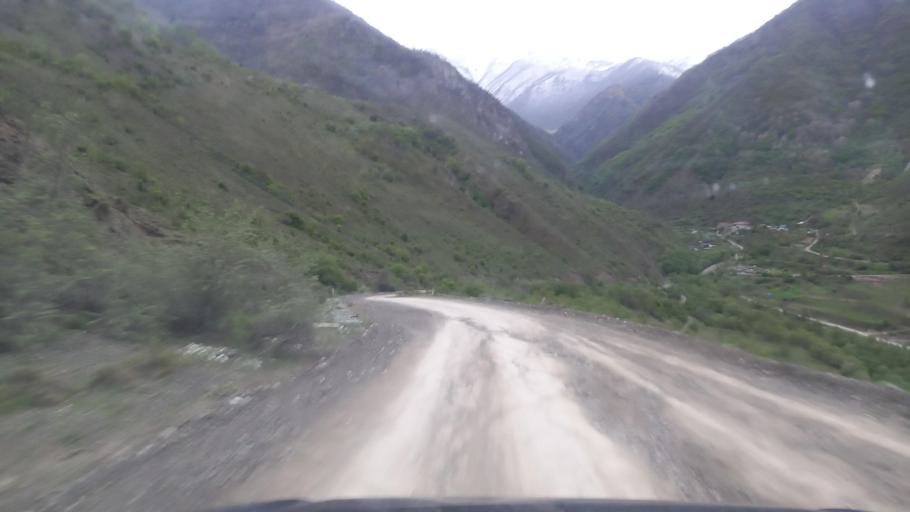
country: RU
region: North Ossetia
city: Mizur
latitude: 42.8554
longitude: 44.1578
